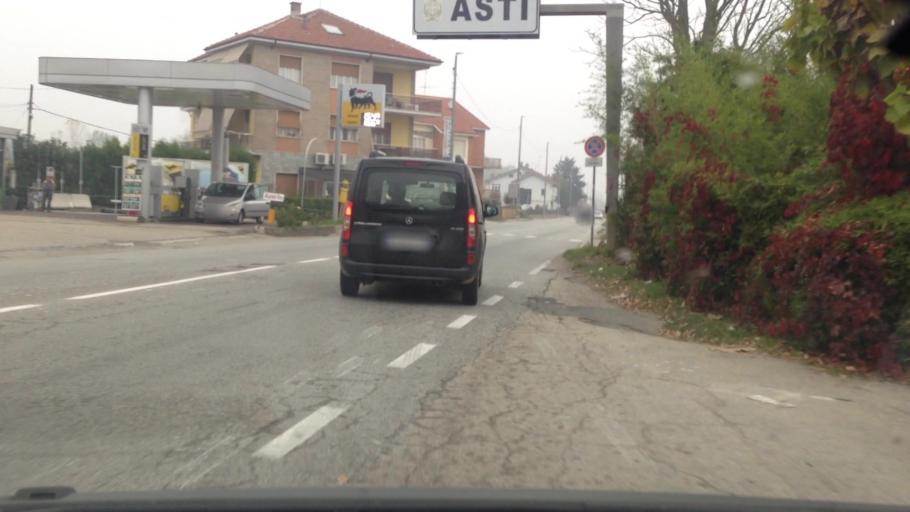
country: IT
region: Piedmont
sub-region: Provincia di Asti
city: Asti
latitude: 44.8771
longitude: 8.2150
